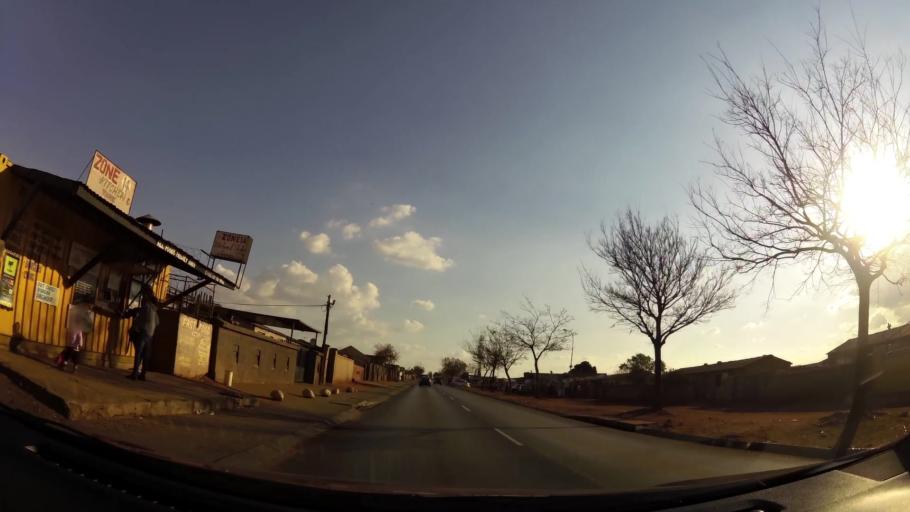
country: ZA
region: Gauteng
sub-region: City of Johannesburg Metropolitan Municipality
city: Soweto
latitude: -26.2259
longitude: 27.8572
